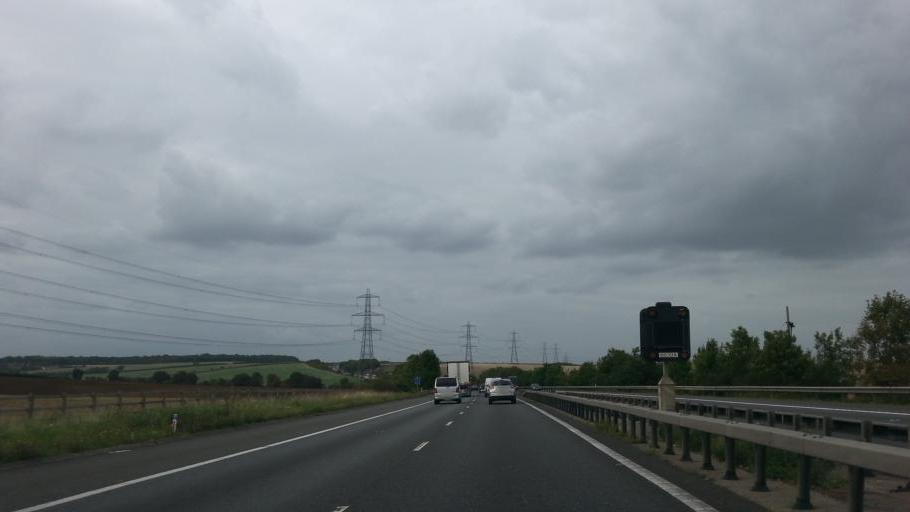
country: GB
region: England
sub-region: Essex
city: Saffron Walden
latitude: 52.0165
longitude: 0.1975
